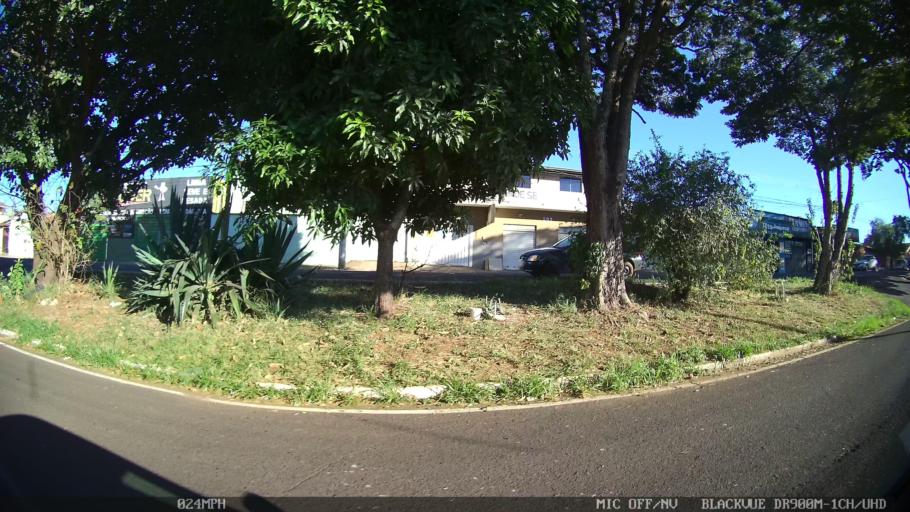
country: BR
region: Sao Paulo
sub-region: Franca
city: Franca
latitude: -20.5778
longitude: -47.3765
